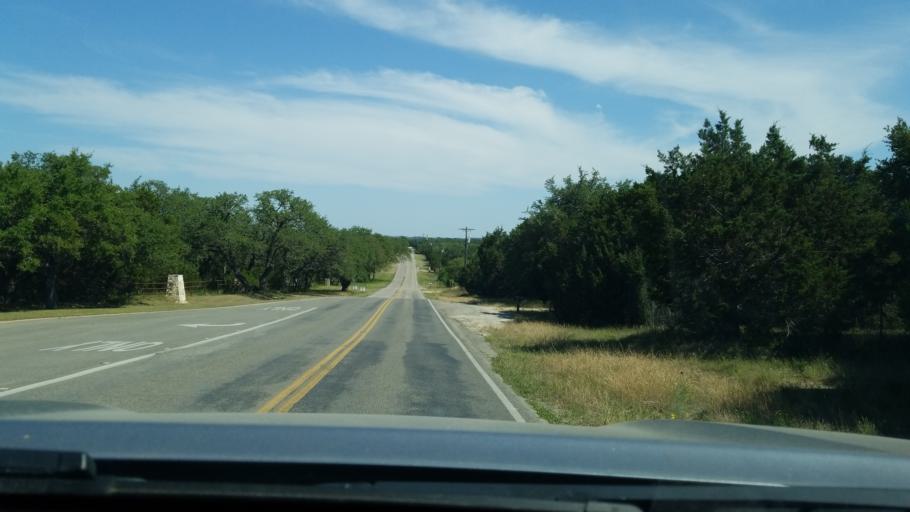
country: US
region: Texas
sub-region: Comal County
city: Bulverde
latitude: 29.7657
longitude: -98.5118
